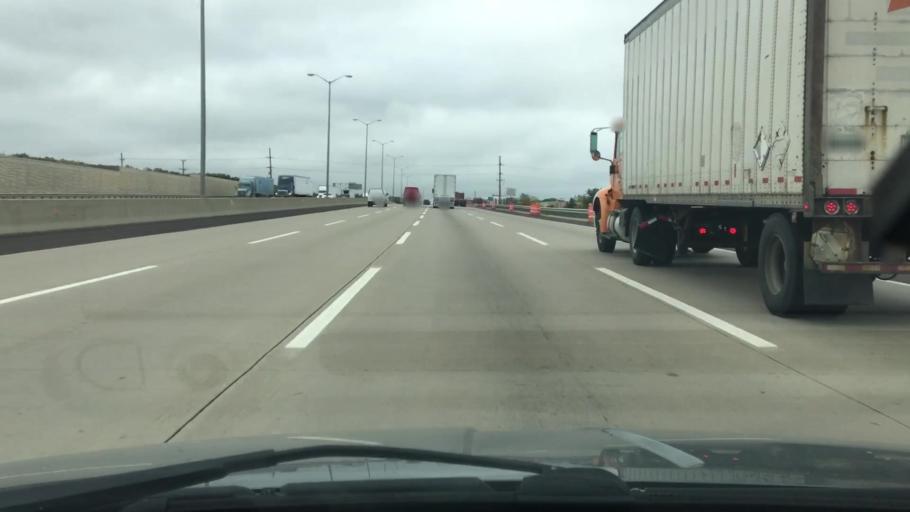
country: US
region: Illinois
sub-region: Cook County
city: Northbrook
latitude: 42.0894
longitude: -87.8679
